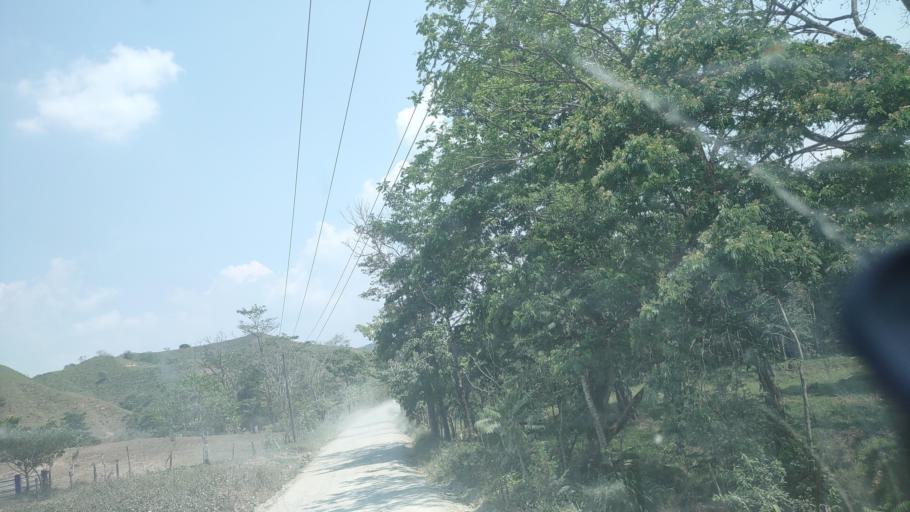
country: MX
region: Tabasco
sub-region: Huimanguillo
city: Francisco Rueda
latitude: 17.5805
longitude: -93.8897
